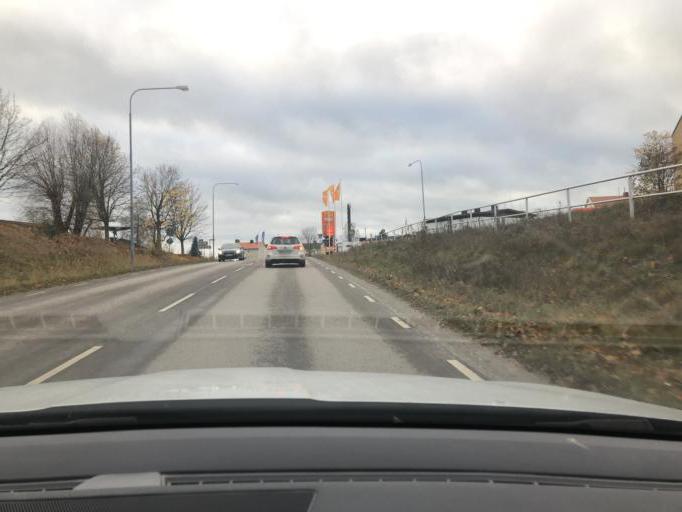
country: SE
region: Uppsala
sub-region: Tierps Kommun
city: Tierp
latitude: 60.3421
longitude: 17.5202
